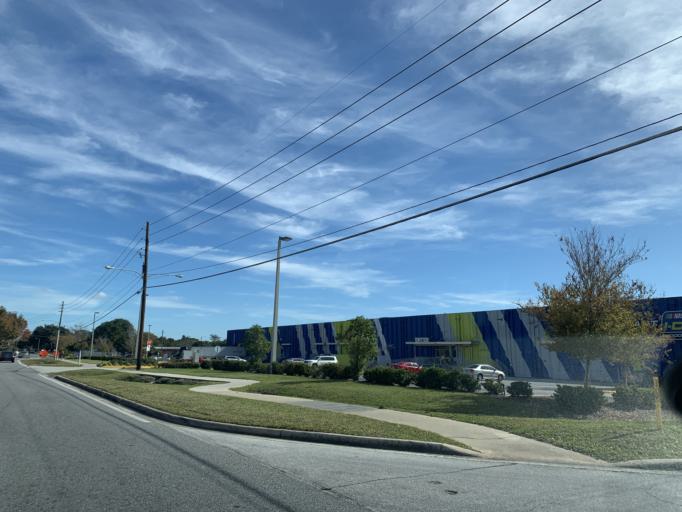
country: US
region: Florida
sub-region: Orange County
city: Tangelo Park
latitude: 28.4612
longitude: -81.4522
